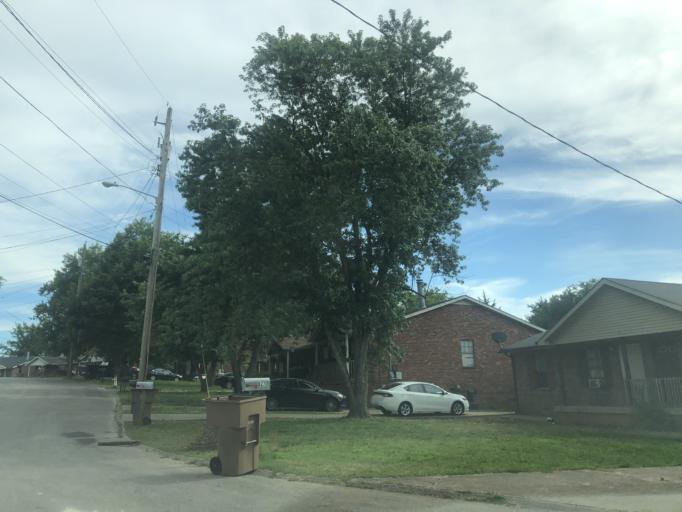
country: US
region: Tennessee
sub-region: Davidson County
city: Nashville
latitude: 36.2240
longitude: -86.8174
